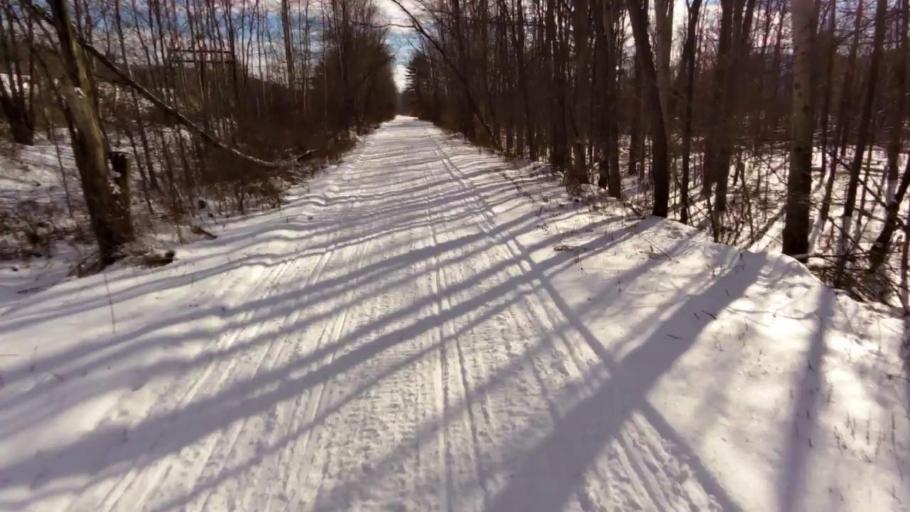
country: US
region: Pennsylvania
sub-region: McKean County
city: Foster Brook
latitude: 42.0121
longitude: -78.6259
